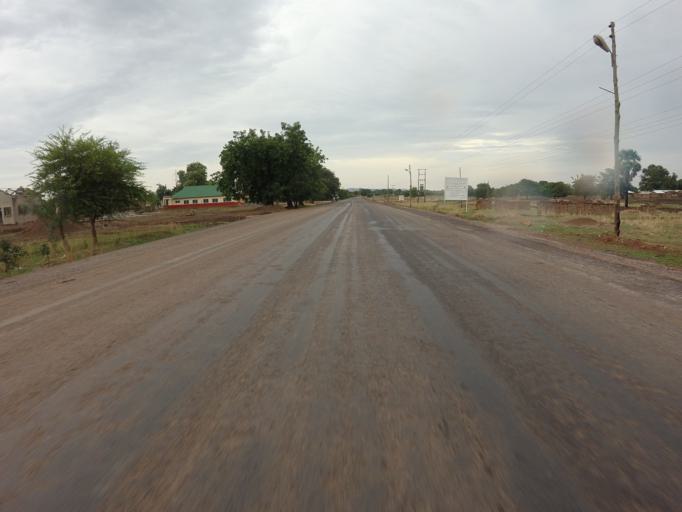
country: GH
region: Upper East
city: Bolgatanga
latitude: 10.8619
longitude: -0.6618
